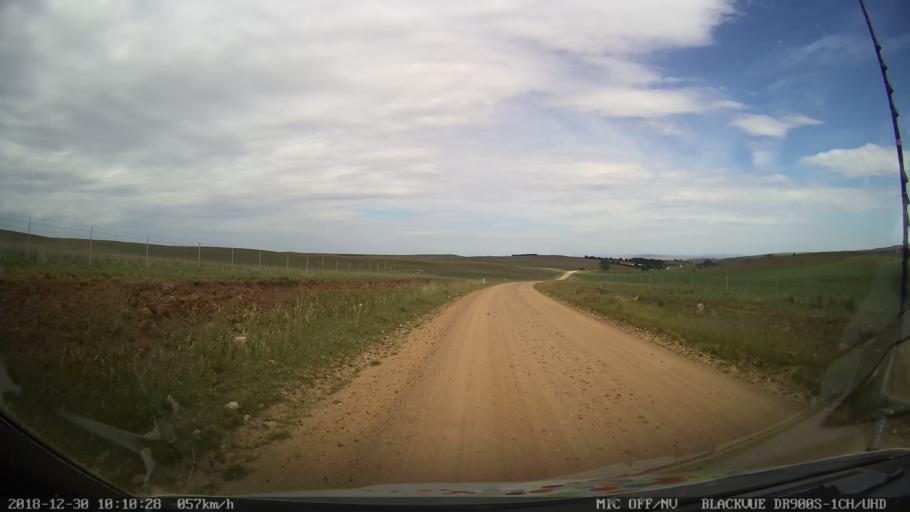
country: AU
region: New South Wales
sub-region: Cooma-Monaro
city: Cooma
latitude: -36.5510
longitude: 149.0945
